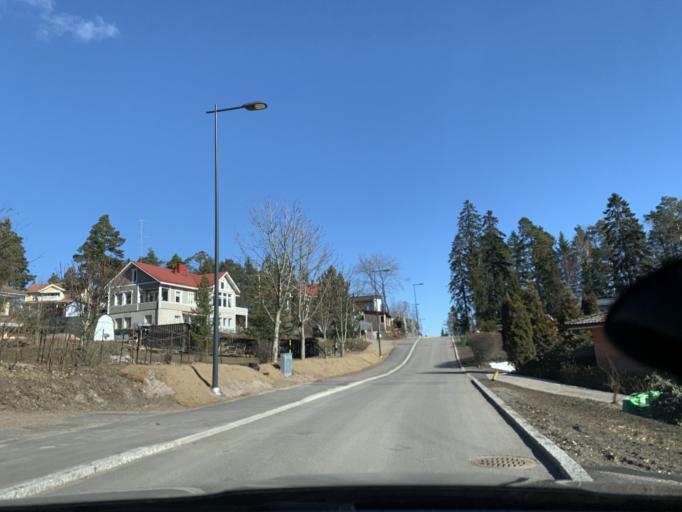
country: FI
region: Uusimaa
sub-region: Helsinki
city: Espoo
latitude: 60.1654
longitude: 24.6028
